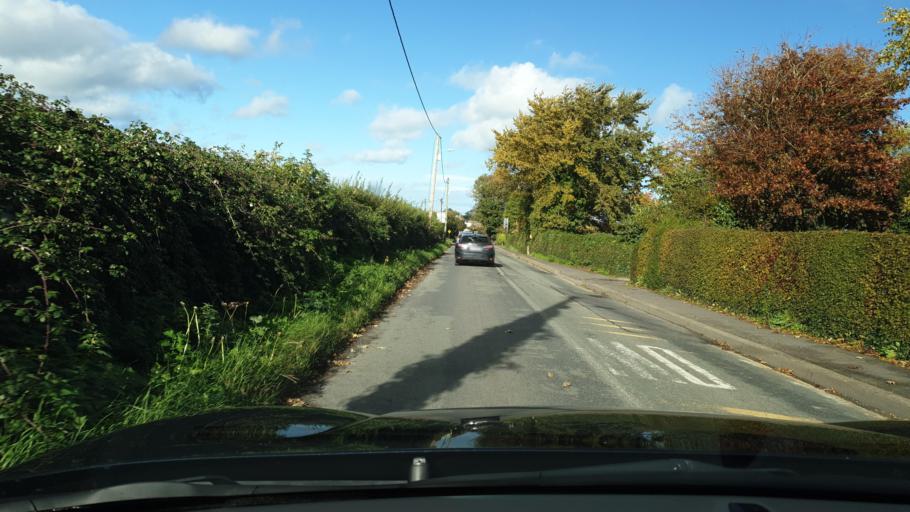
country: IE
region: Leinster
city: An Ros
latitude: 53.5478
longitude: -6.1014
